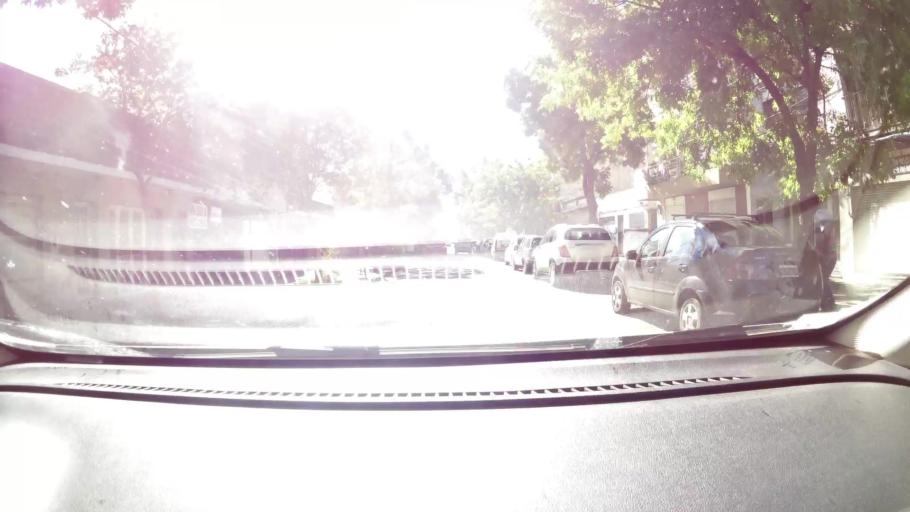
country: AR
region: Santa Fe
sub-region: Departamento de Rosario
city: Rosario
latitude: -32.9513
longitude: -60.6677
